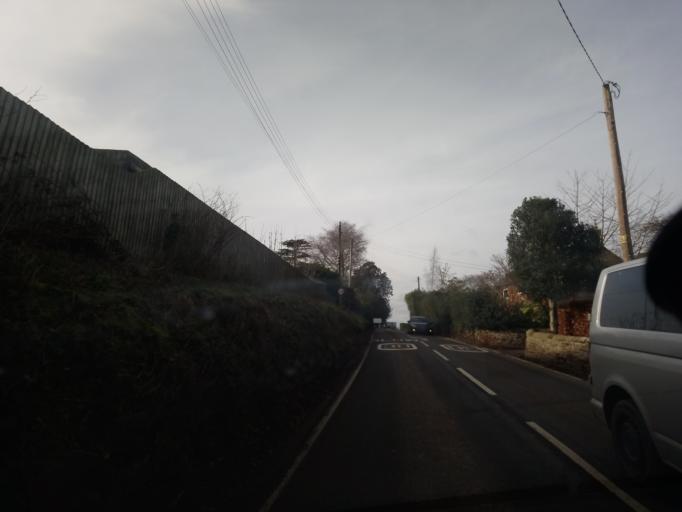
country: GB
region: England
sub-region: Shropshire
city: Stoke upon Tern
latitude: 52.8613
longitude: -2.5994
